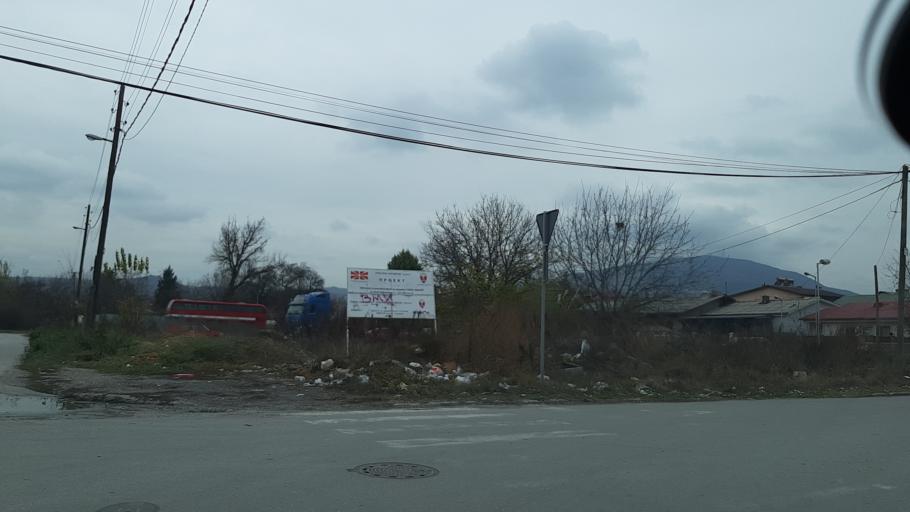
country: MK
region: Kisela Voda
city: Usje
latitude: 41.9744
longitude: 21.4792
